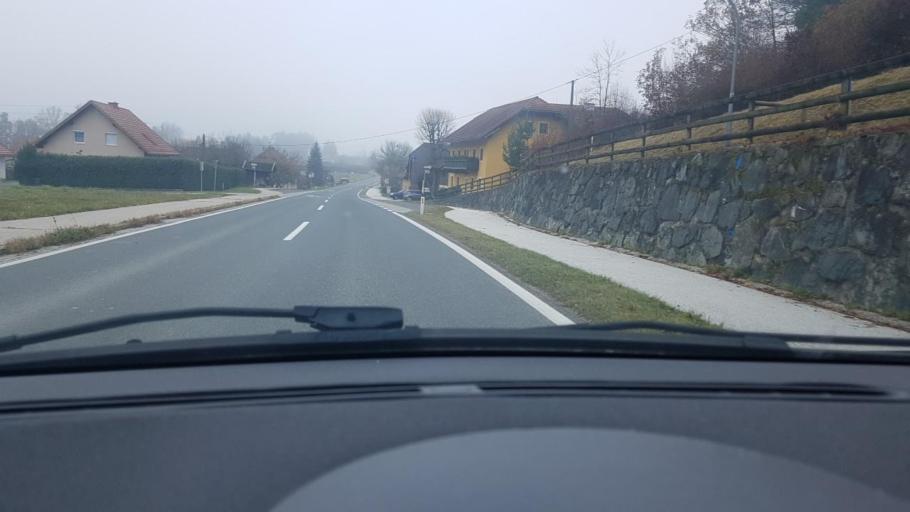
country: AT
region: Carinthia
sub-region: Politischer Bezirk Volkermarkt
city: Bleiburg/Pliberk
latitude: 46.6118
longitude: 14.8005
